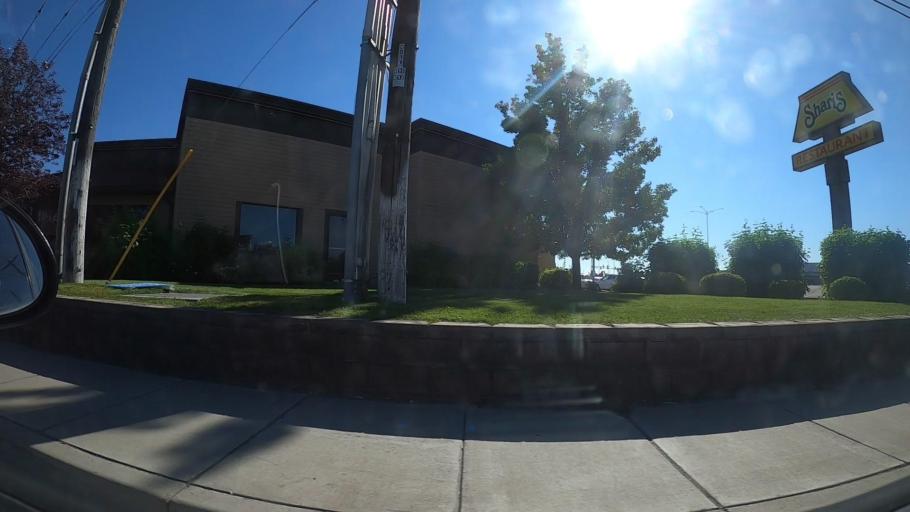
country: US
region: Idaho
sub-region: Canyon County
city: Nampa
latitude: 43.6073
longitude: -116.6056
